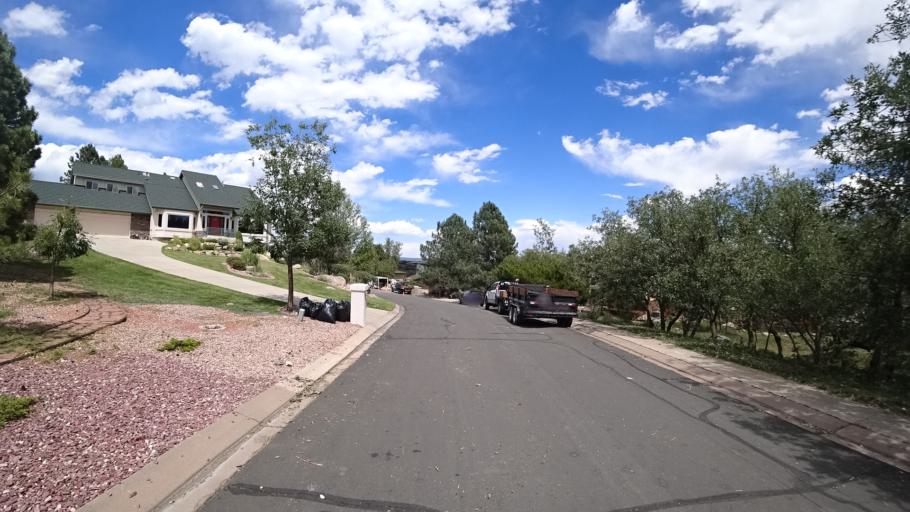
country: US
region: Colorado
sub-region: El Paso County
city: Stratmoor
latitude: 38.7743
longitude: -104.8349
